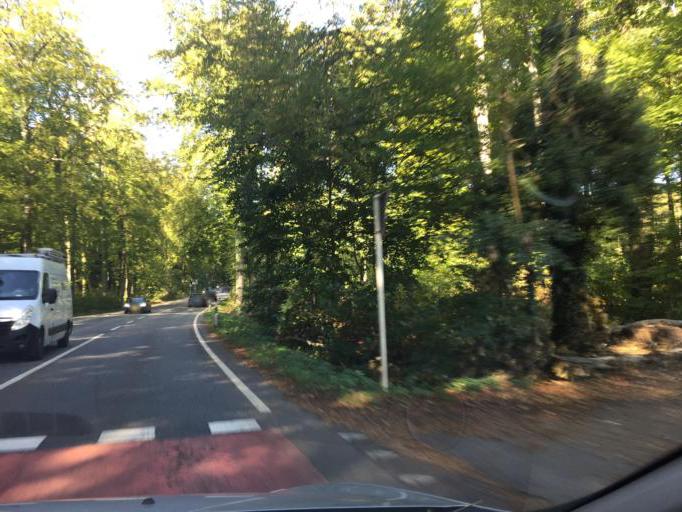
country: LU
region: Luxembourg
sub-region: Canton de Luxembourg
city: Strassen
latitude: 49.6365
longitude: 6.0663
